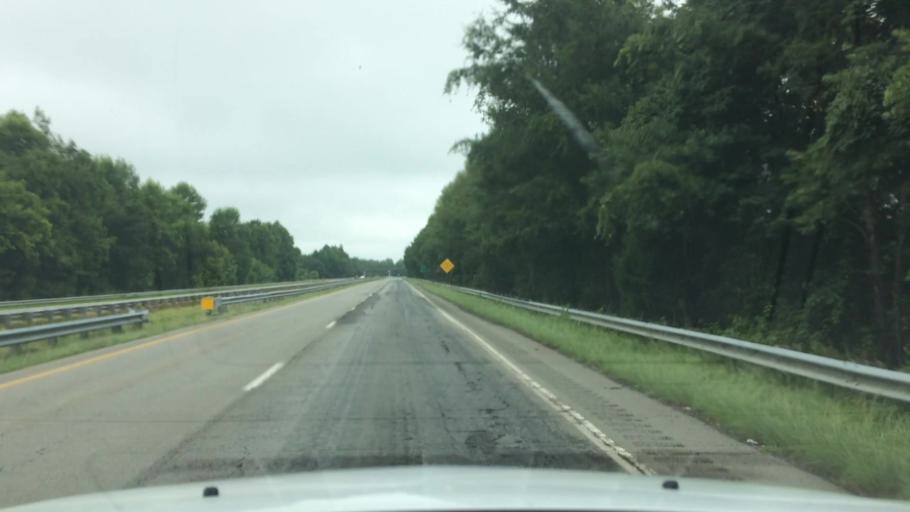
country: US
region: North Carolina
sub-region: Forsyth County
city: Lewisville
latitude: 36.1045
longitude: -80.5117
